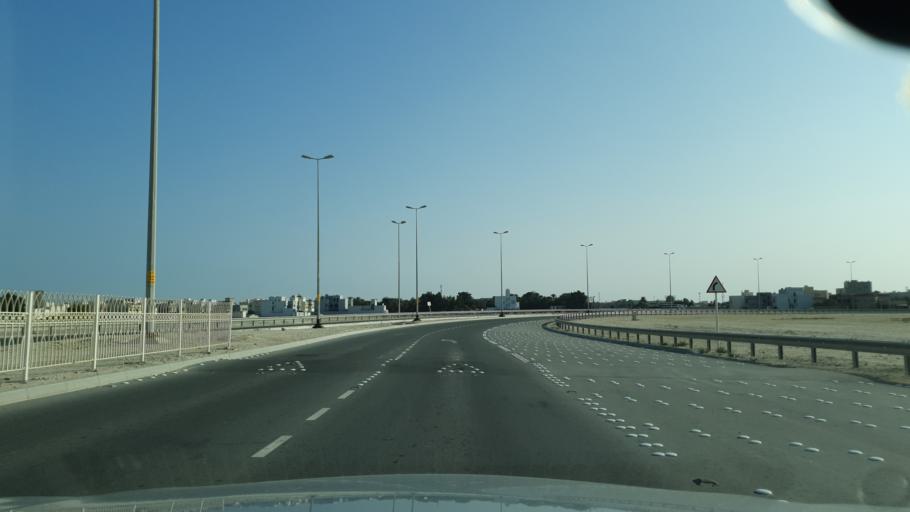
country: BH
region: Manama
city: Jidd Hafs
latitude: 26.2337
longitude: 50.4618
